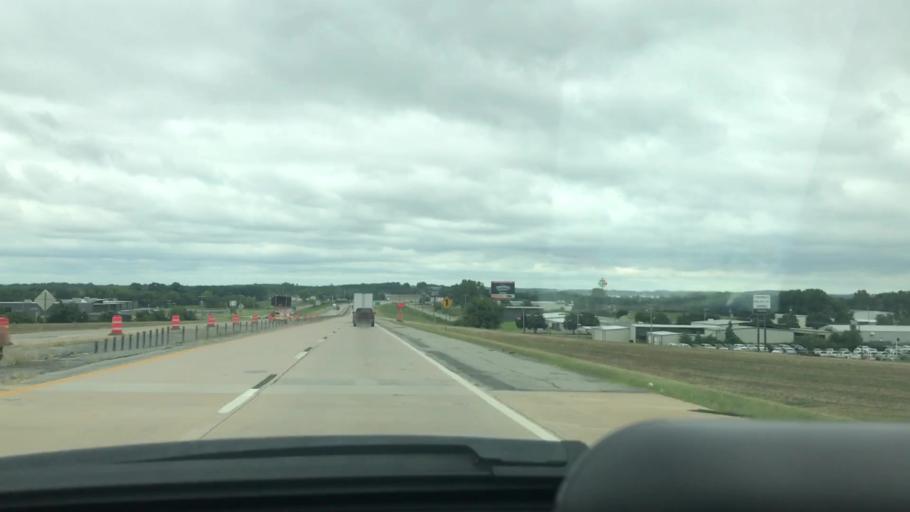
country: US
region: Oklahoma
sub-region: McIntosh County
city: Eufaula
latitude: 35.2951
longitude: -95.5931
